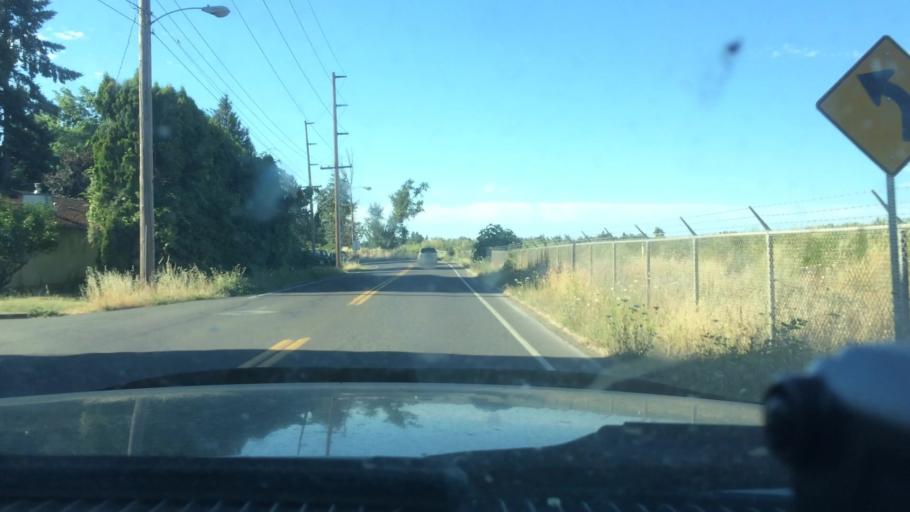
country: US
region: Oregon
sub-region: Lane County
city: Eugene
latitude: 44.1000
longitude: -123.1142
